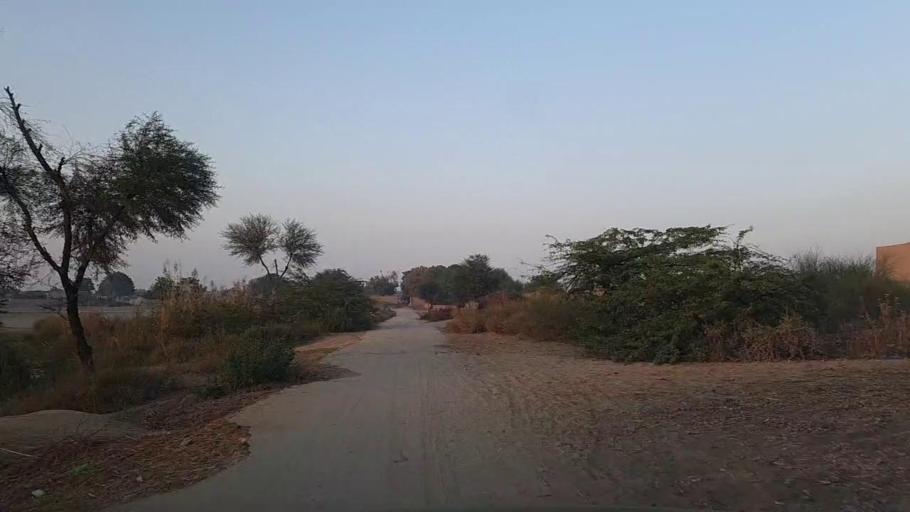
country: PK
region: Sindh
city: Jam Sahib
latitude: 26.4720
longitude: 68.5423
